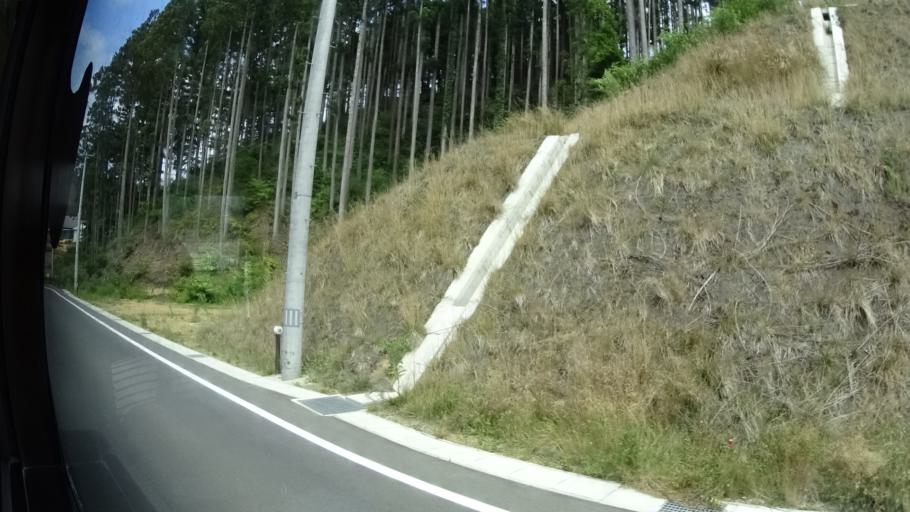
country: JP
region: Miyagi
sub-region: Oshika Gun
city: Onagawa Cho
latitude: 38.6801
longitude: 141.4566
